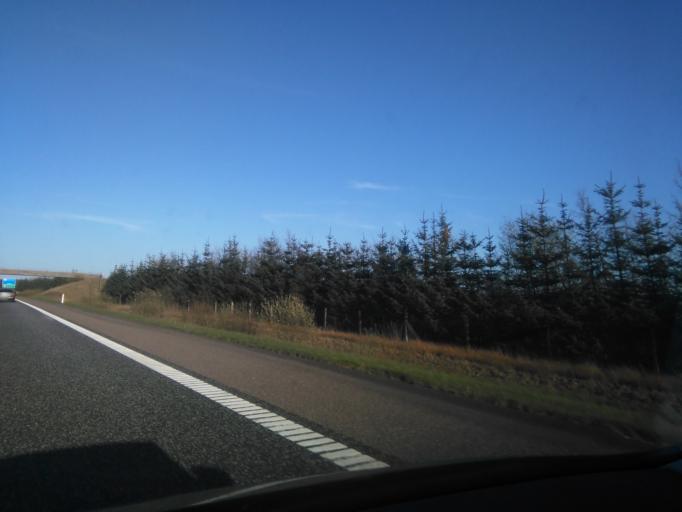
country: DK
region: Central Jutland
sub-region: Ikast-Brande Kommune
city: Ikast
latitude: 56.1163
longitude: 9.1493
